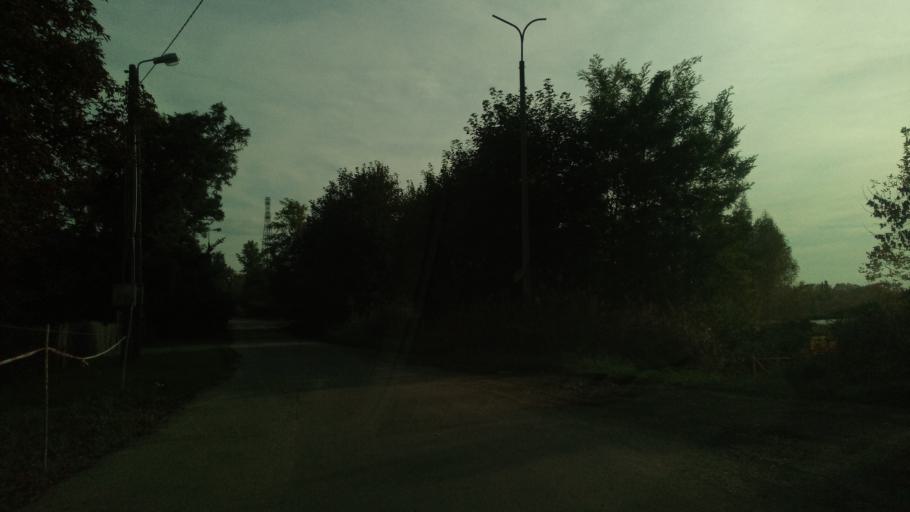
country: PL
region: Silesian Voivodeship
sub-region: Sosnowiec
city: Sosnowiec
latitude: 50.2631
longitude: 19.1268
